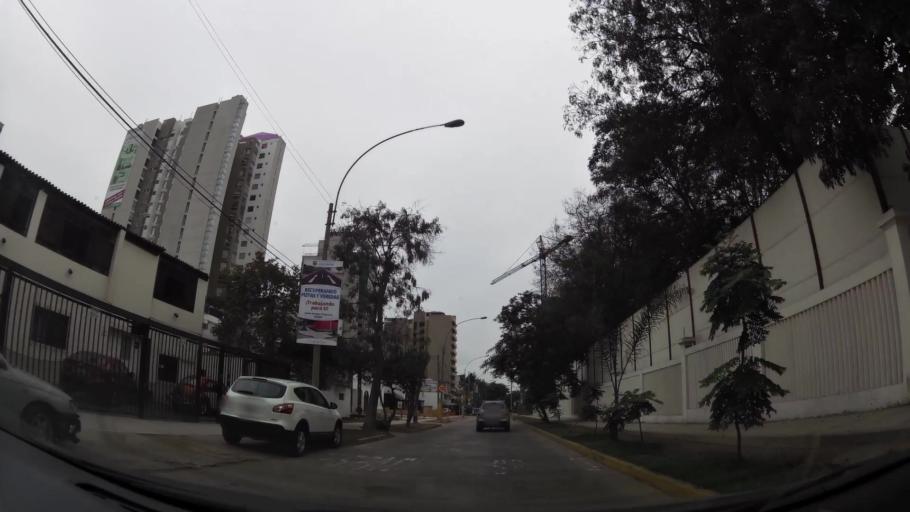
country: PE
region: Lima
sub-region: Lima
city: San Isidro
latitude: -12.0812
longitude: -77.0460
